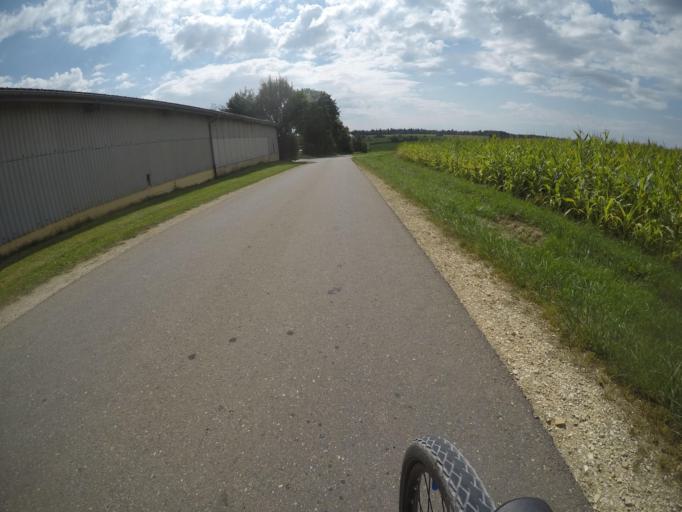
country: DE
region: Baden-Wuerttemberg
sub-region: Tuebingen Region
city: Munsingen
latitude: 48.4280
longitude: 9.4951
